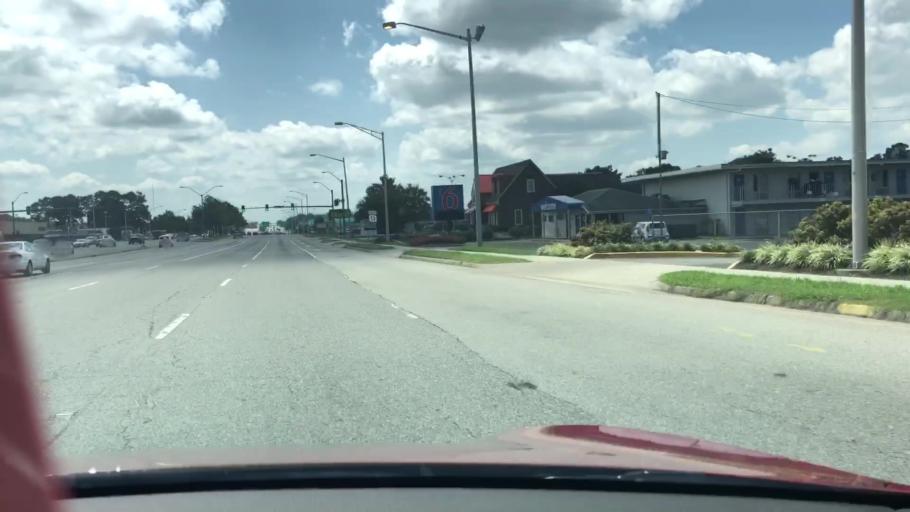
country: US
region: Virginia
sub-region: City of Chesapeake
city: Chesapeake
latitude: 36.8531
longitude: -76.2102
